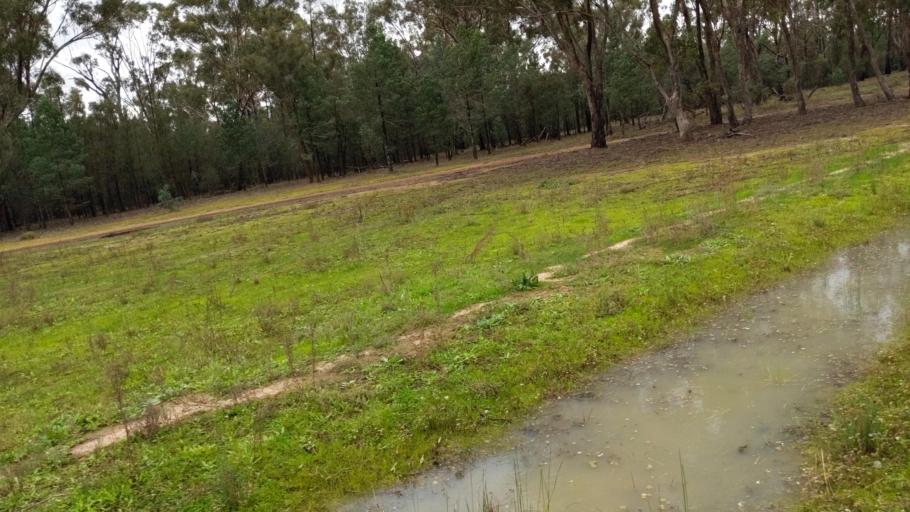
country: AU
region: New South Wales
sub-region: Coolamon
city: Coolamon
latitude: -34.8601
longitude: 146.9241
